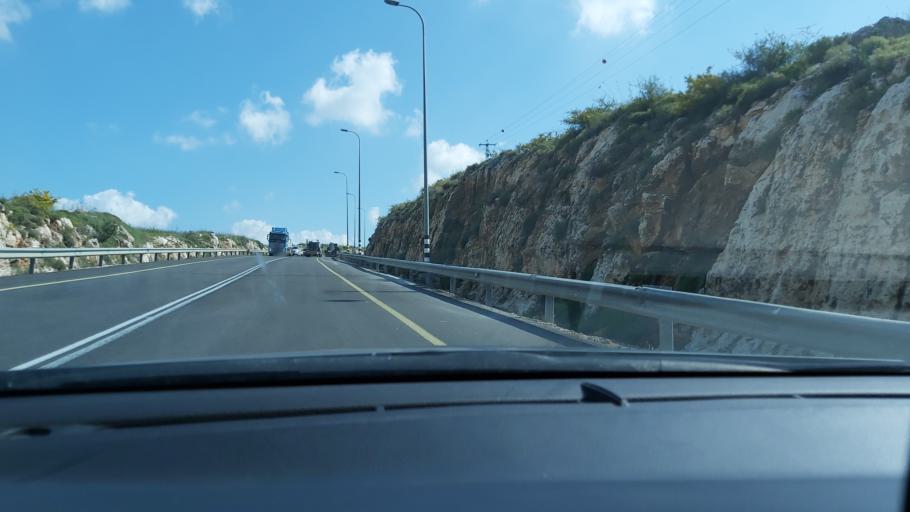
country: PS
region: West Bank
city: Bruqin
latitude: 32.0871
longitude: 35.1035
